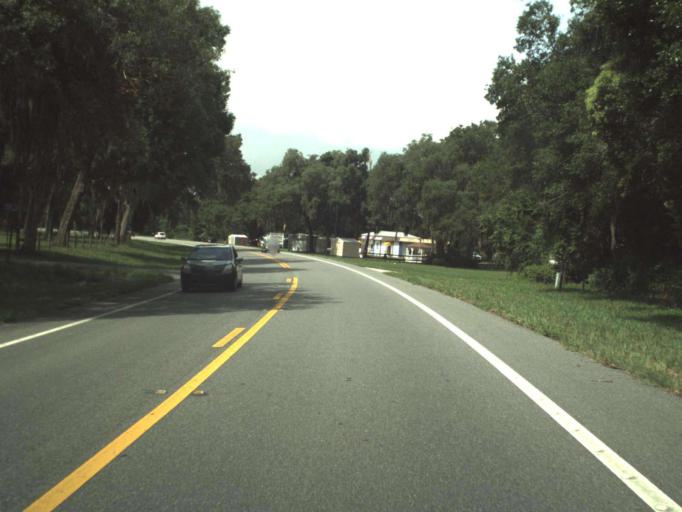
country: US
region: Florida
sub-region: Sumter County
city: Bushnell
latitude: 28.7091
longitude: -82.1028
